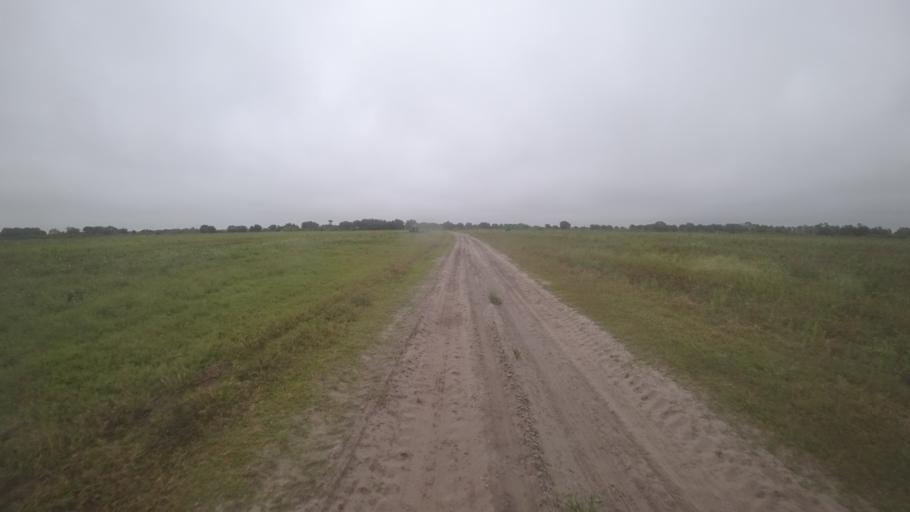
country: US
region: Florida
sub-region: Sarasota County
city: The Meadows
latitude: 27.4428
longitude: -82.3403
